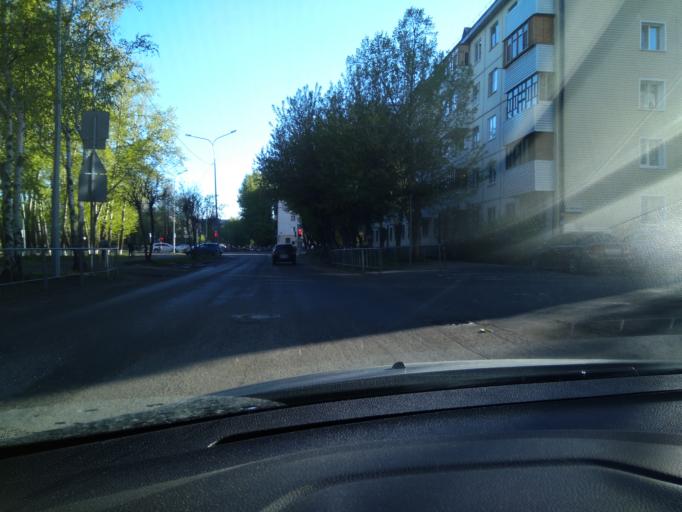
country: RU
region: Tjumen
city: Tyumen
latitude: 57.1321
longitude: 65.5887
